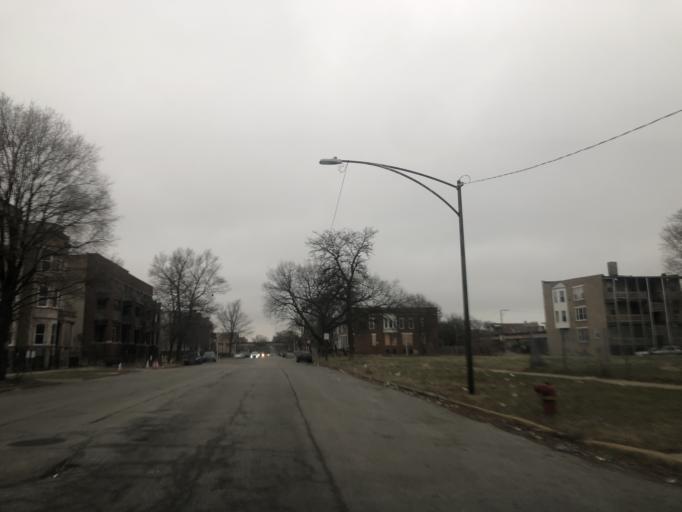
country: US
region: Illinois
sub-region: Cook County
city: Chicago
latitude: 41.7846
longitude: -87.6189
